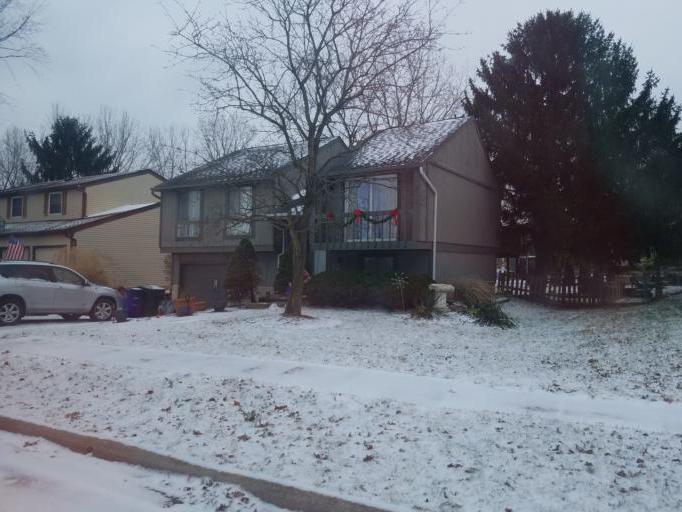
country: US
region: Ohio
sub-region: Delaware County
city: Powell
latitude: 40.1380
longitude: -83.0655
